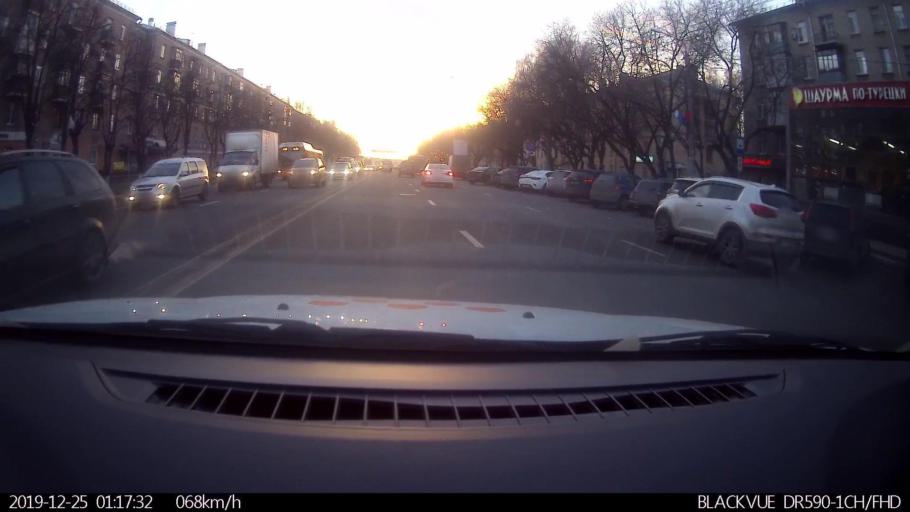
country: RU
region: Nizjnij Novgorod
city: Nizhniy Novgorod
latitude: 56.2653
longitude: 43.9120
